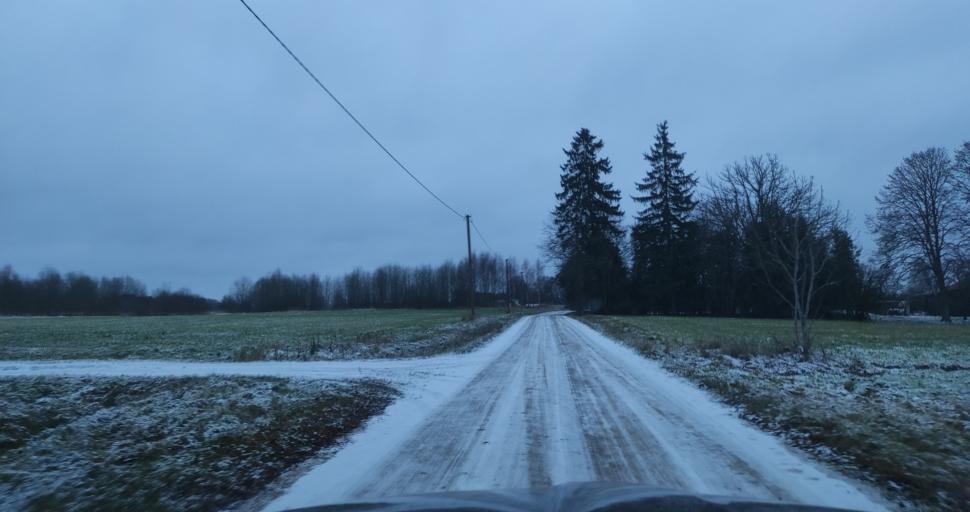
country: LV
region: Kuldigas Rajons
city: Kuldiga
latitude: 56.9757
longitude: 22.0546
